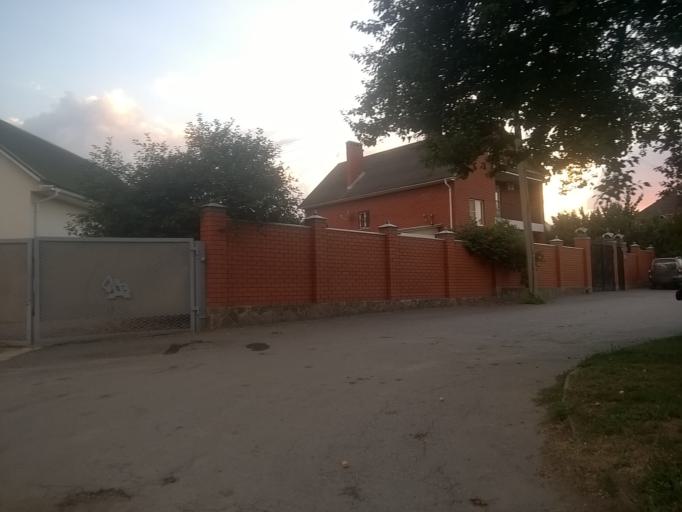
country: RU
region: Rostov
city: Donetsk
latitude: 48.3317
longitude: 39.9575
